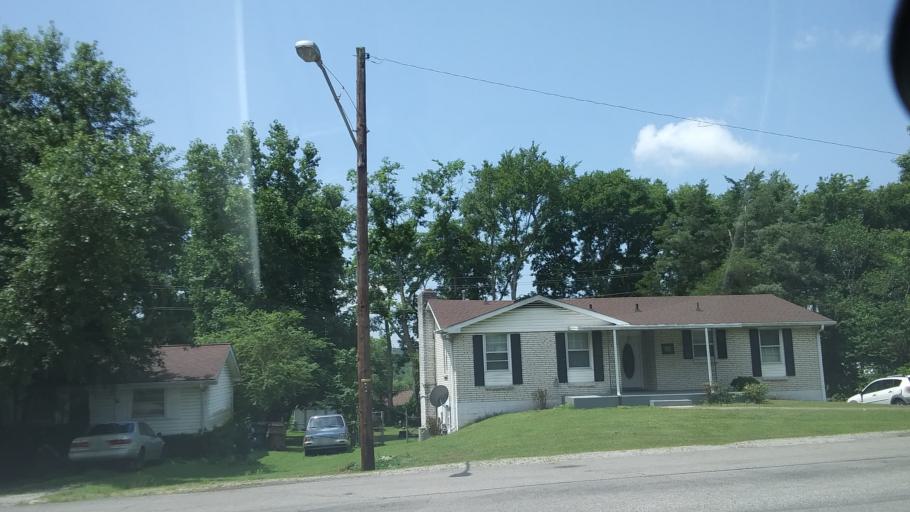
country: US
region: Tennessee
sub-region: Davidson County
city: Belle Meade
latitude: 36.1455
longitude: -86.8840
